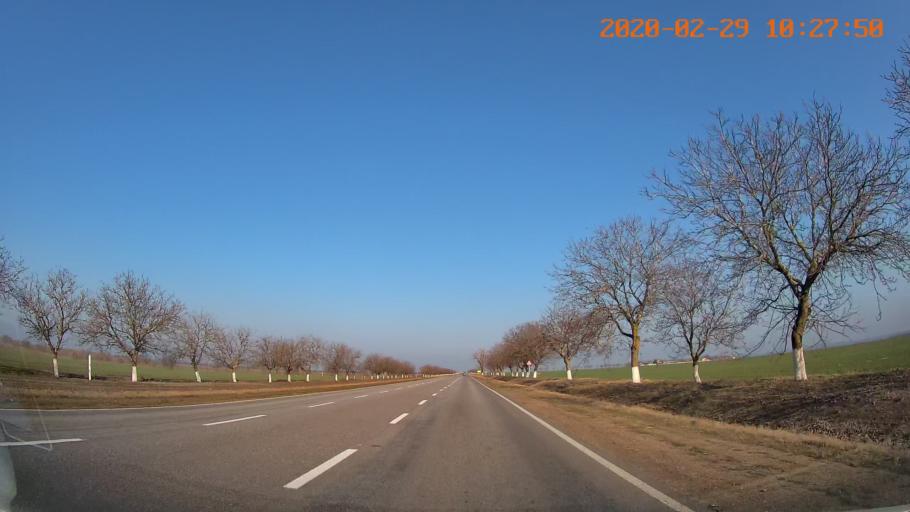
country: MD
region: Telenesti
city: Tiraspolul Nou
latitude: 46.9019
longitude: 29.5952
